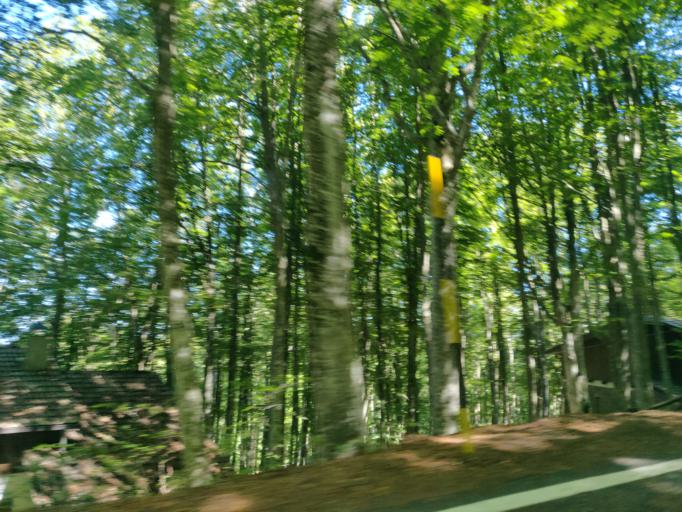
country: IT
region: Tuscany
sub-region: Provincia di Siena
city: Abbadia San Salvatore
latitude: 42.8972
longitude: 11.6281
